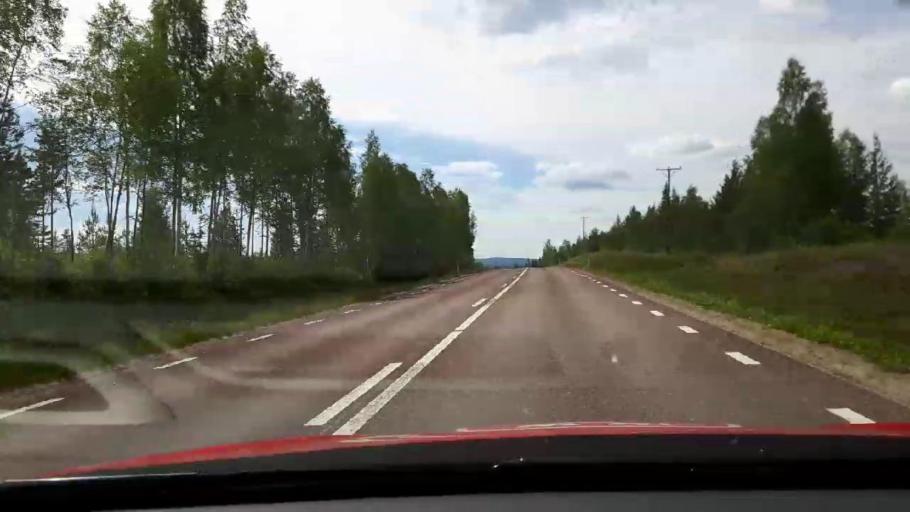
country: SE
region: Jaemtland
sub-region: Harjedalens Kommun
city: Sveg
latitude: 62.0631
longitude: 14.9177
